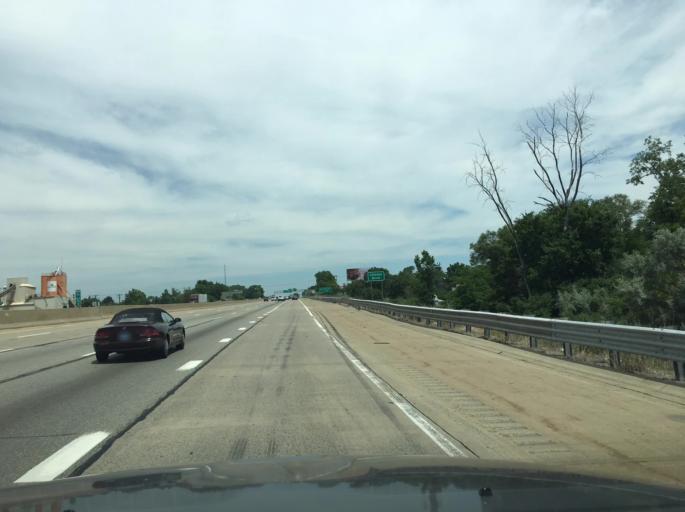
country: US
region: Michigan
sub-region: Oakland County
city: Bloomfield Hills
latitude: 42.6314
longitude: -83.2385
